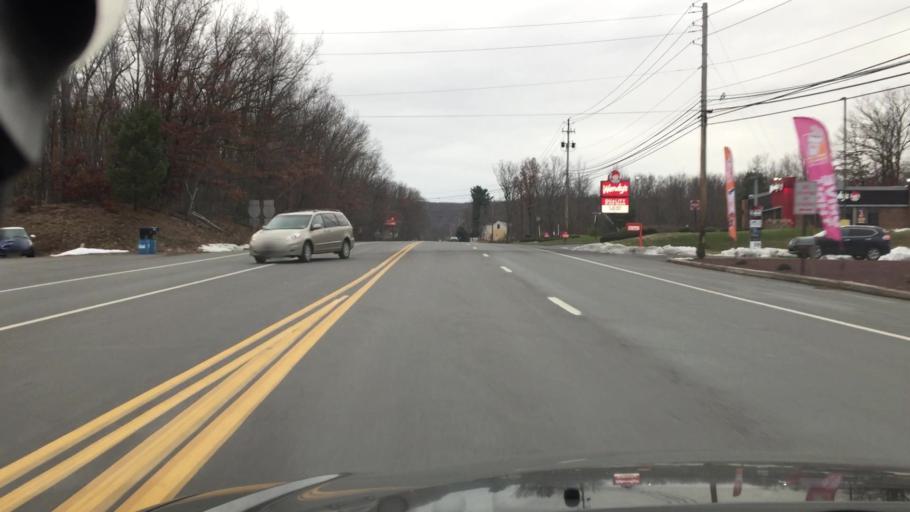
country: US
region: Pennsylvania
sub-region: Luzerne County
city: Freeland
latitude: 41.0553
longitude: -75.9606
